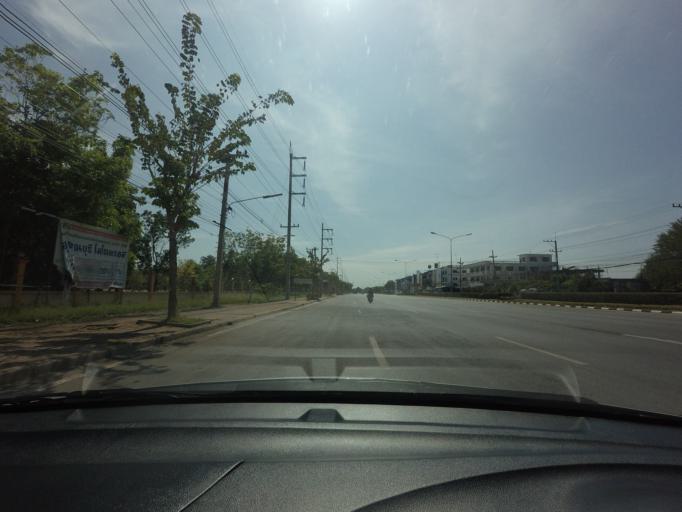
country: TH
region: Suphan Buri
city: Dan Chang
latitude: 14.8405
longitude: 99.6959
